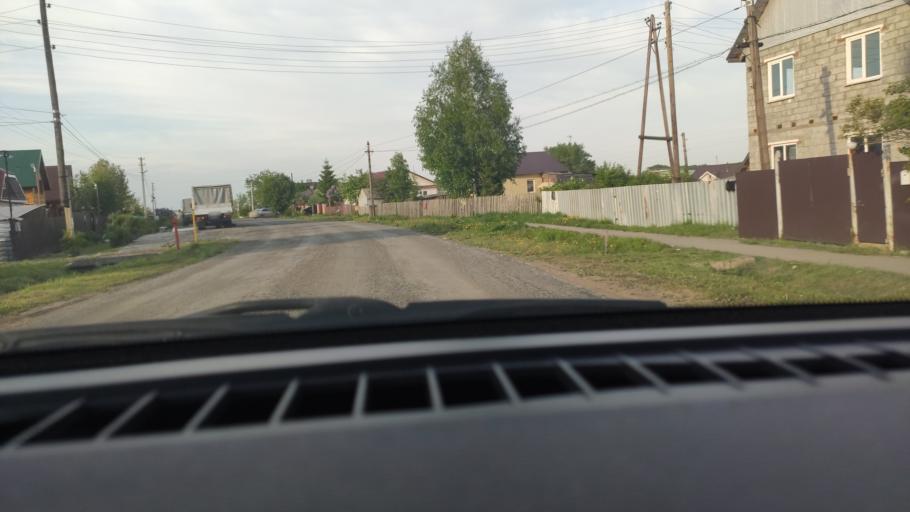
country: RU
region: Perm
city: Kondratovo
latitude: 57.9360
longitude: 56.0262
